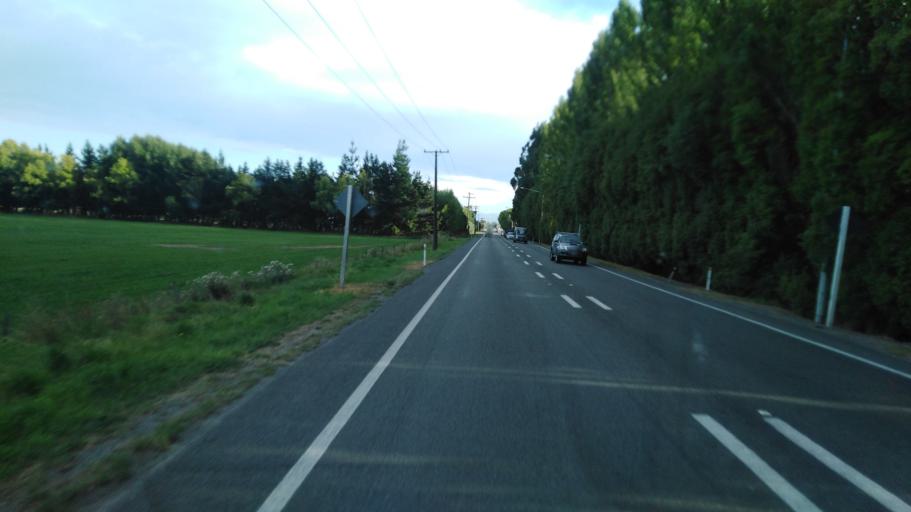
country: NZ
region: Canterbury
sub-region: Waimakariri District
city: Woodend
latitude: -43.3380
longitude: 172.6667
